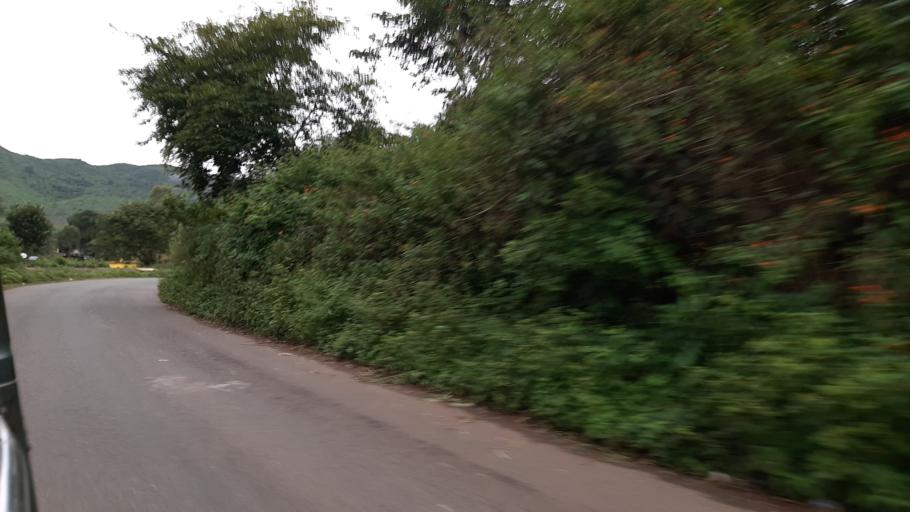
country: IN
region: Andhra Pradesh
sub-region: Vizianagaram District
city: Salur
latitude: 18.2838
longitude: 82.9405
